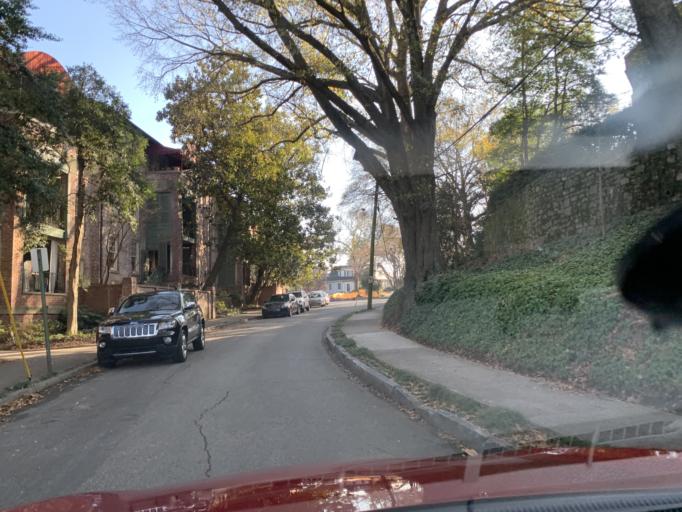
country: US
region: Georgia
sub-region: Fulton County
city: Atlanta
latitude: 33.7896
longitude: -84.3787
